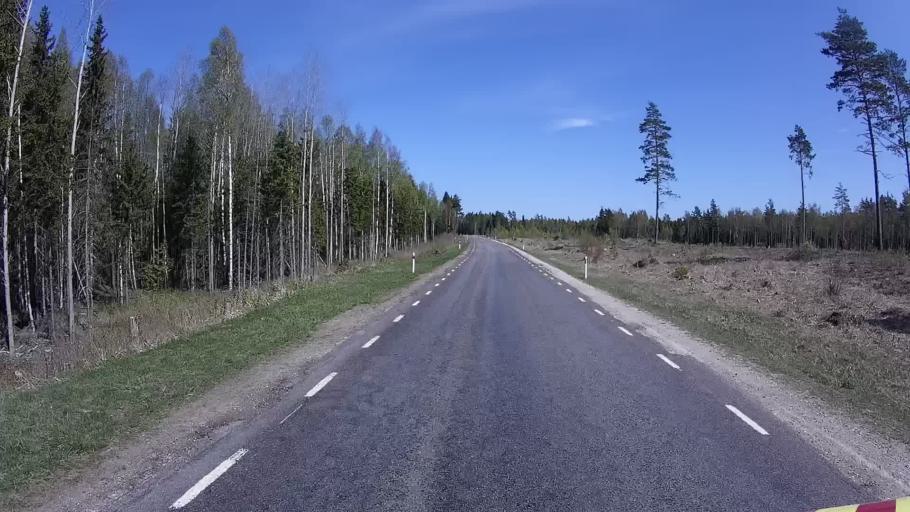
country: EE
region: Harju
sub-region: Nissi vald
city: Turba
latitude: 59.1048
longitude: 24.0355
